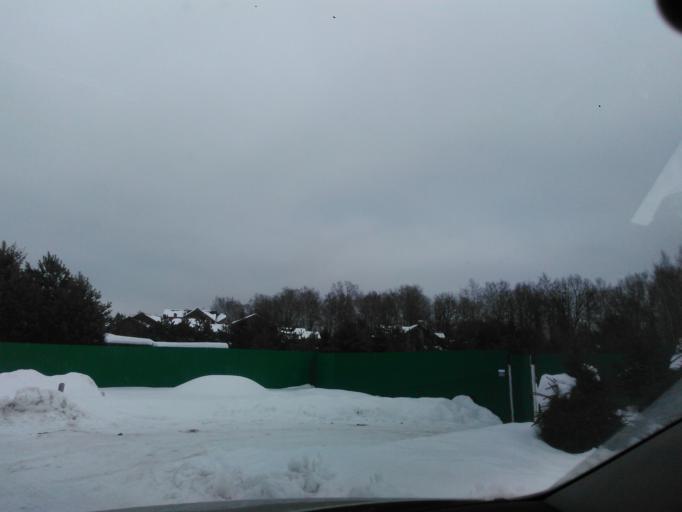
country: RU
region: Moskovskaya
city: Podosinki
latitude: 56.2727
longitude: 37.6257
